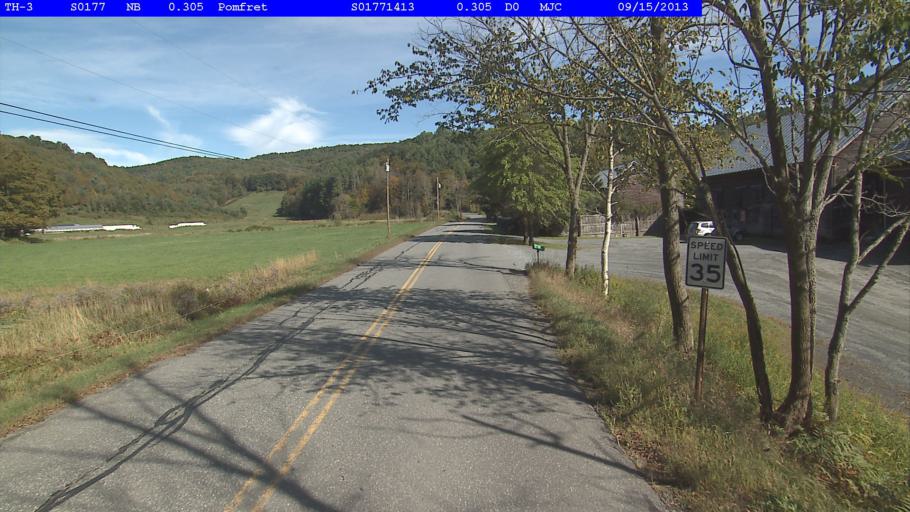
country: US
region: Vermont
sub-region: Windsor County
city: Woodstock
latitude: 43.7273
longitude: -72.4976
